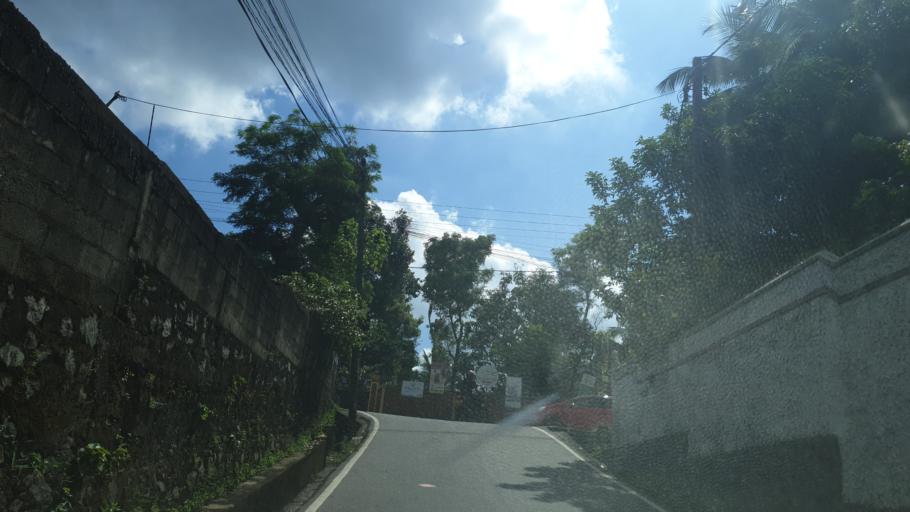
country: LK
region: Western
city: Moratuwa
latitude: 6.7928
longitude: 79.9106
